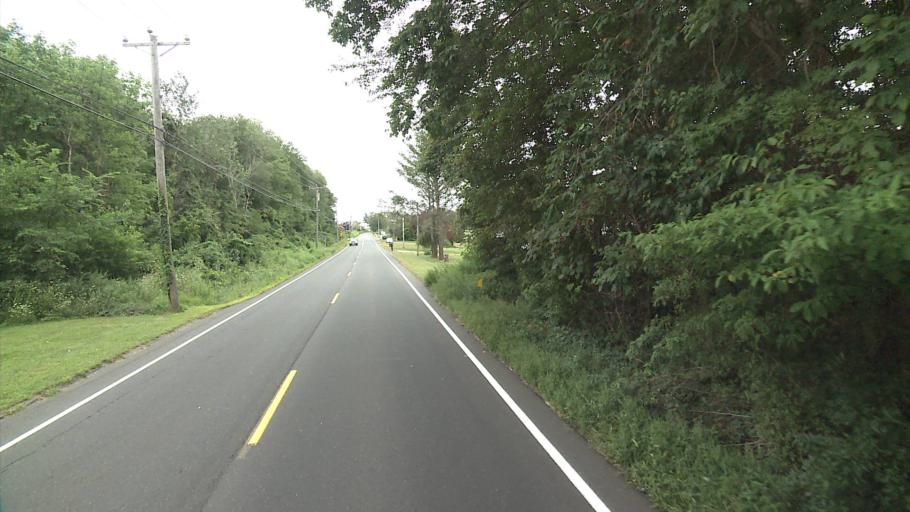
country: US
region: Connecticut
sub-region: New London County
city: Colchester
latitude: 41.5359
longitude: -72.3006
